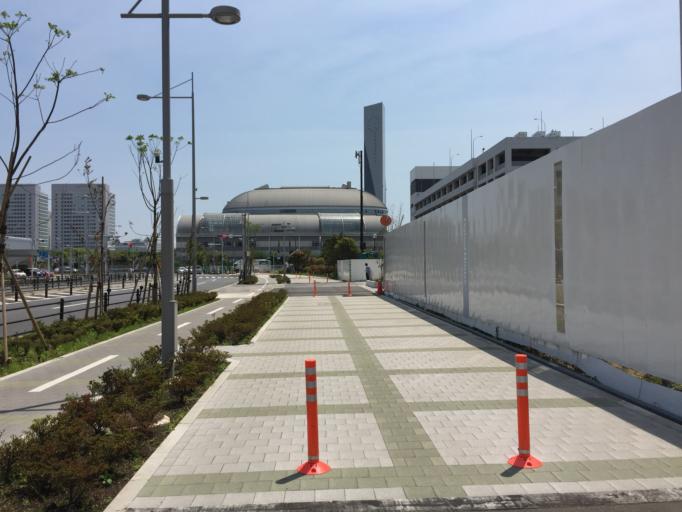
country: JP
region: Tokyo
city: Tokyo
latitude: 35.6360
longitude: 139.7814
